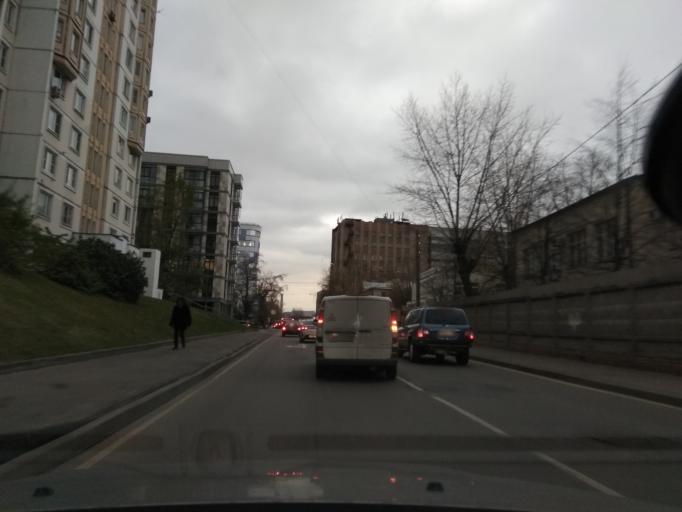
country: RU
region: Moscow
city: Mar'ina Roshcha
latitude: 55.7979
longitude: 37.6012
